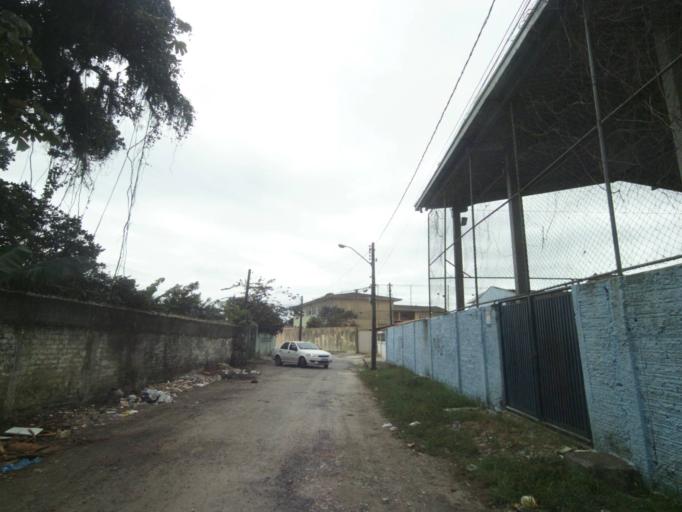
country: BR
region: Parana
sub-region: Paranagua
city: Paranagua
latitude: -25.5194
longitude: -48.5319
